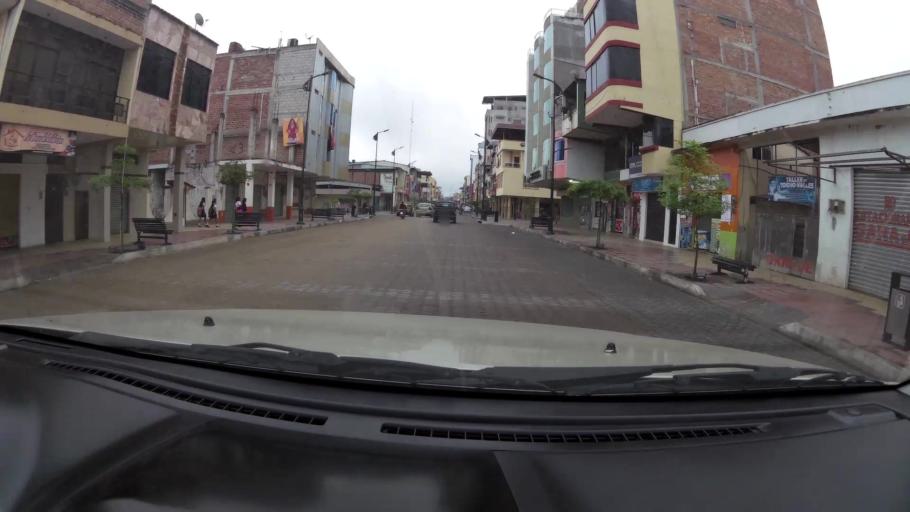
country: EC
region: El Oro
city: Pasaje
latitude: -3.3280
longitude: -79.8105
